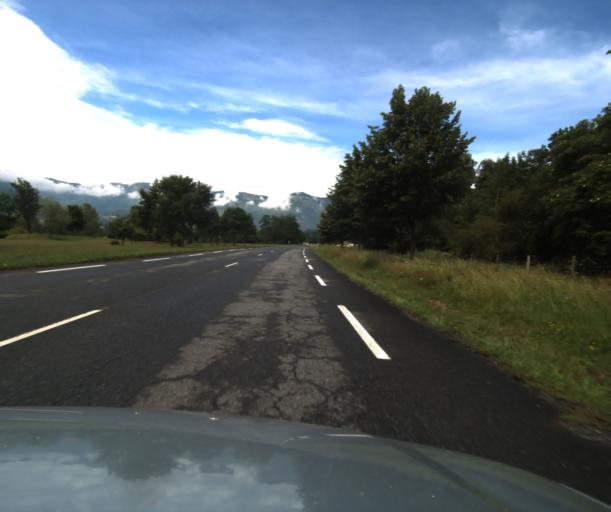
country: FR
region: Midi-Pyrenees
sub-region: Departement des Hautes-Pyrenees
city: Pierrefitte-Nestalas
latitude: 42.9841
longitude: -0.0715
